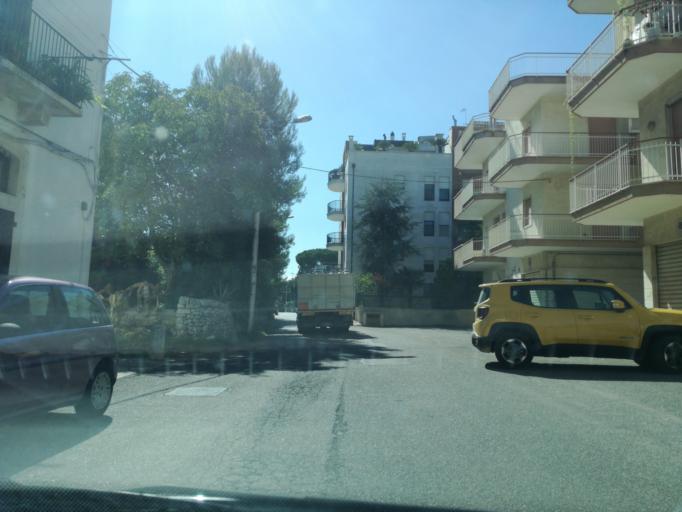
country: IT
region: Apulia
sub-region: Provincia di Bari
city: Castellana
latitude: 40.8900
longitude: 17.1661
